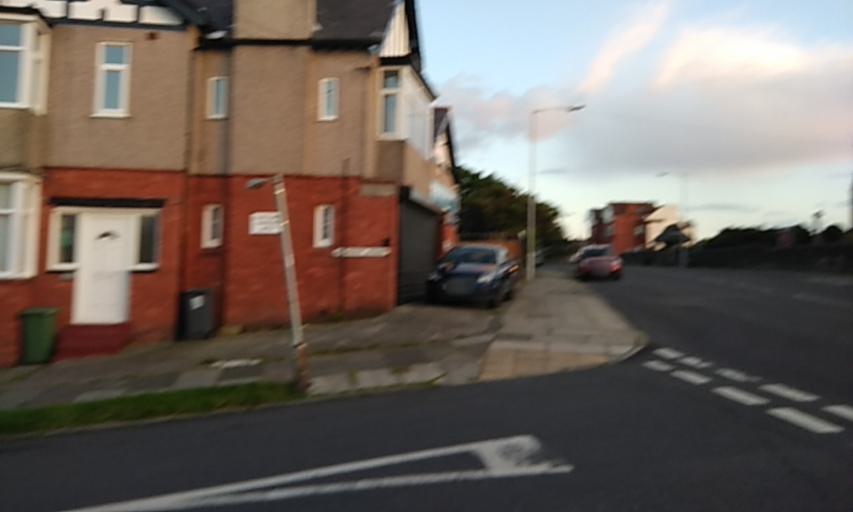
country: GB
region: England
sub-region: Metropolitan Borough of Wirral
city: Wallasey
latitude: 53.4222
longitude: -3.0596
